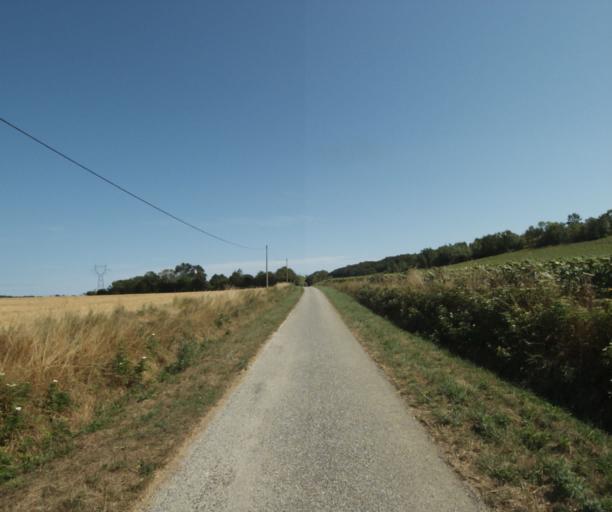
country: FR
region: Midi-Pyrenees
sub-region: Departement de la Haute-Garonne
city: Saint-Felix-Lauragais
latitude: 43.4468
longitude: 1.8403
